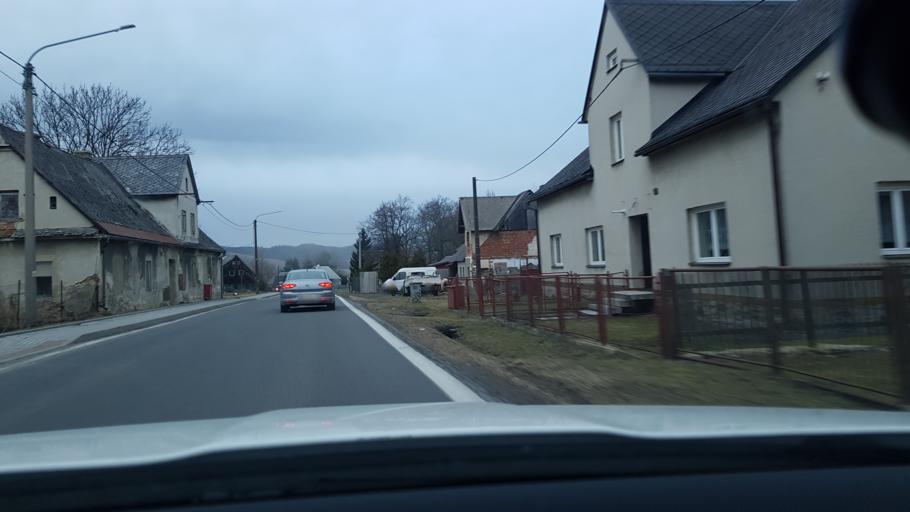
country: CZ
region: Olomoucky
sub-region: Okres Jesenik
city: Jesenik
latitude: 50.1835
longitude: 17.1981
